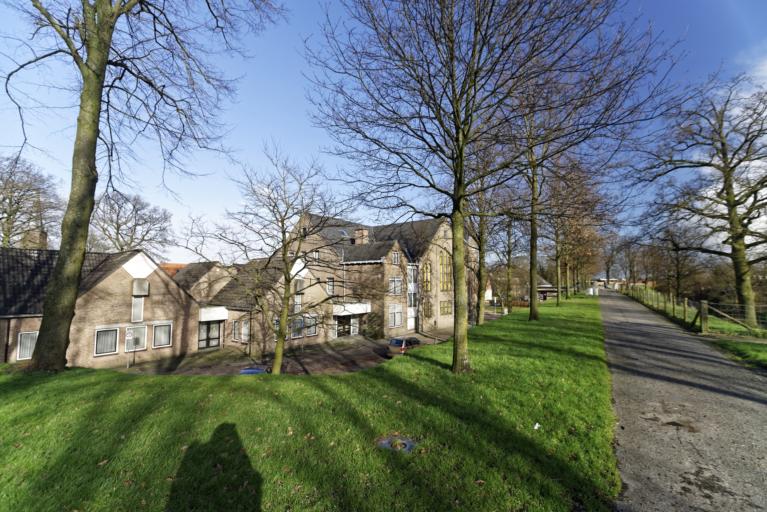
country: NL
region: Overijssel
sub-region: Gemeente Steenwijkerland
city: Steenwijk
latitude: 52.7848
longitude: 6.1170
